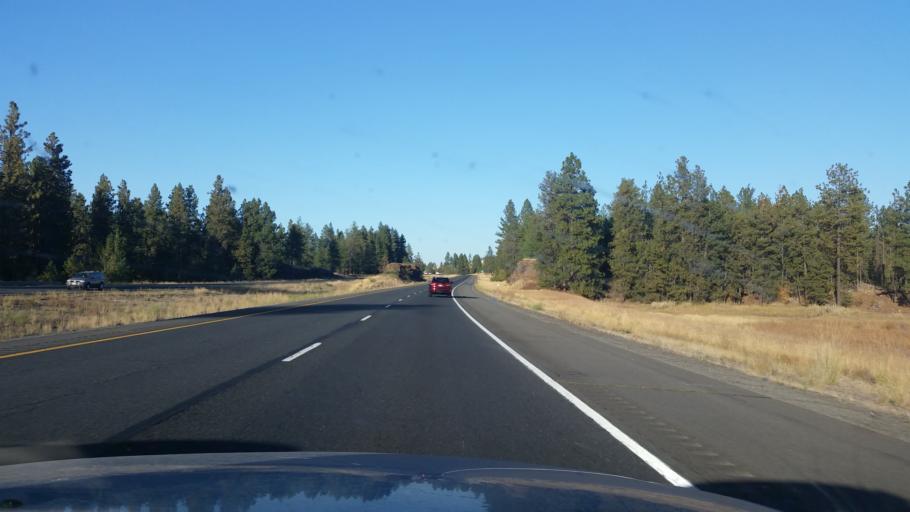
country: US
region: Washington
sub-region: Spokane County
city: Medical Lake
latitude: 47.5290
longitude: -117.6569
